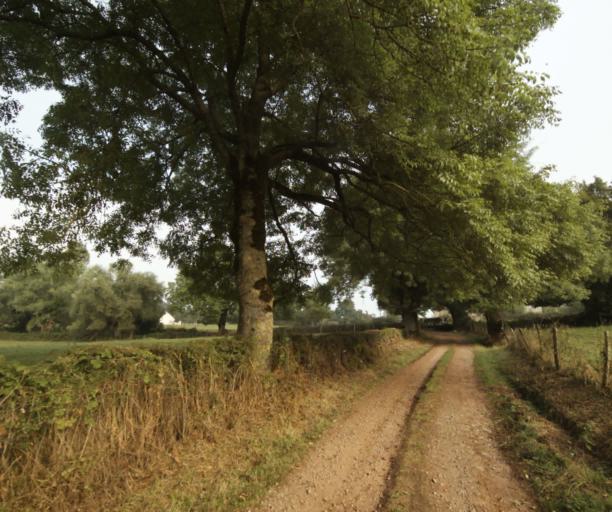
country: FR
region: Bourgogne
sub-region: Departement de Saone-et-Loire
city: Charolles
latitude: 46.4522
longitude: 4.2893
